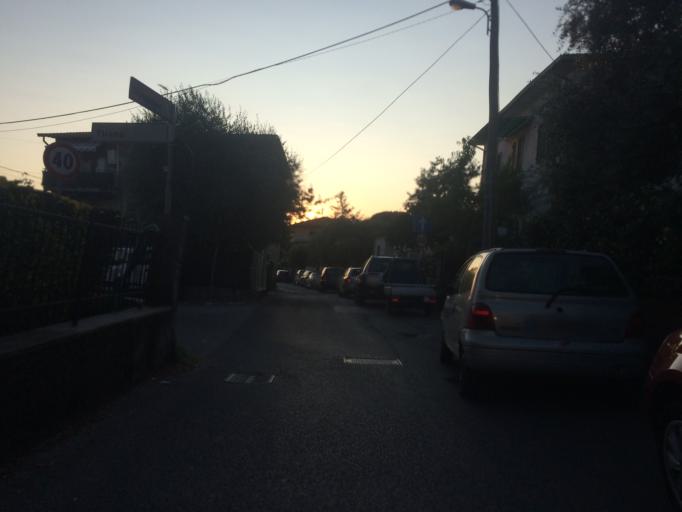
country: IT
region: Tuscany
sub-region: Provincia di Massa-Carrara
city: Massa
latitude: 44.0396
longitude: 10.1186
